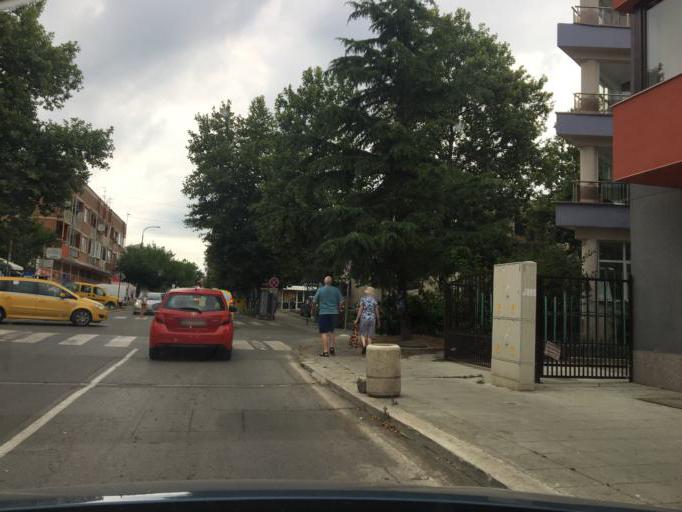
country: BG
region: Burgas
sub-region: Obshtina Sozopol
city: Sozopol
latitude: 42.4144
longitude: 27.6972
